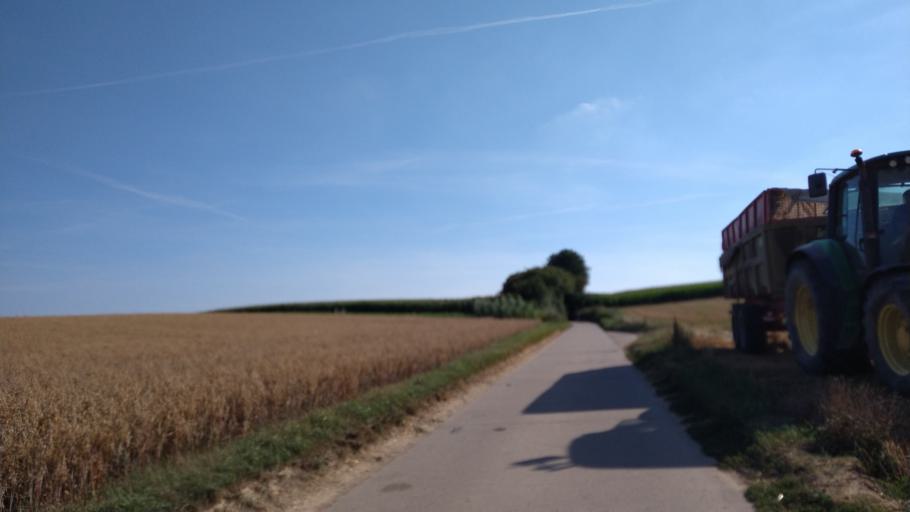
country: BE
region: Flanders
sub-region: Provincie Vlaams-Brabant
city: Bertem
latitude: 50.8464
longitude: 4.6214
